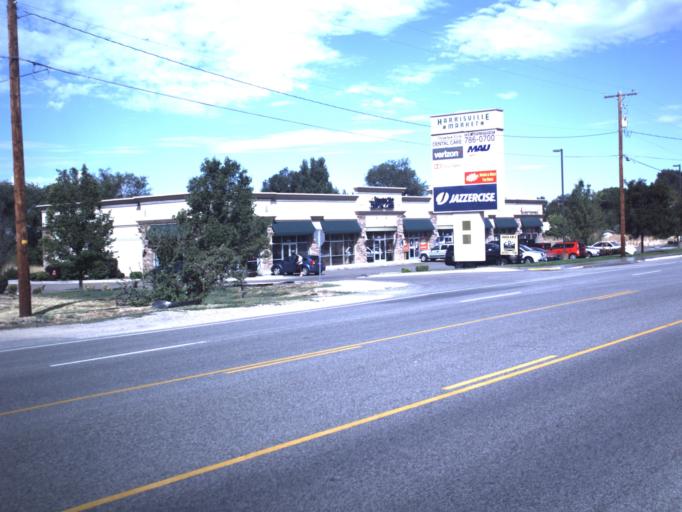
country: US
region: Utah
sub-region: Weber County
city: Harrisville
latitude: 41.2682
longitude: -111.9752
